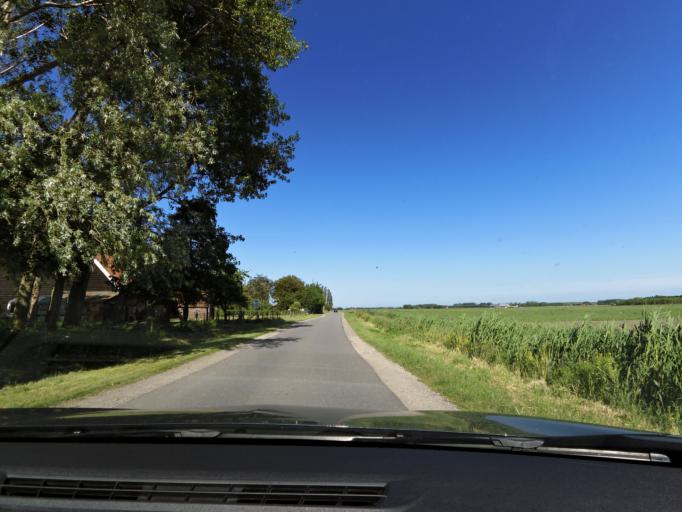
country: NL
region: South Holland
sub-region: Gemeente Hellevoetsluis
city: Nieuwenhoorn
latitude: 51.8635
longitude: 4.1262
